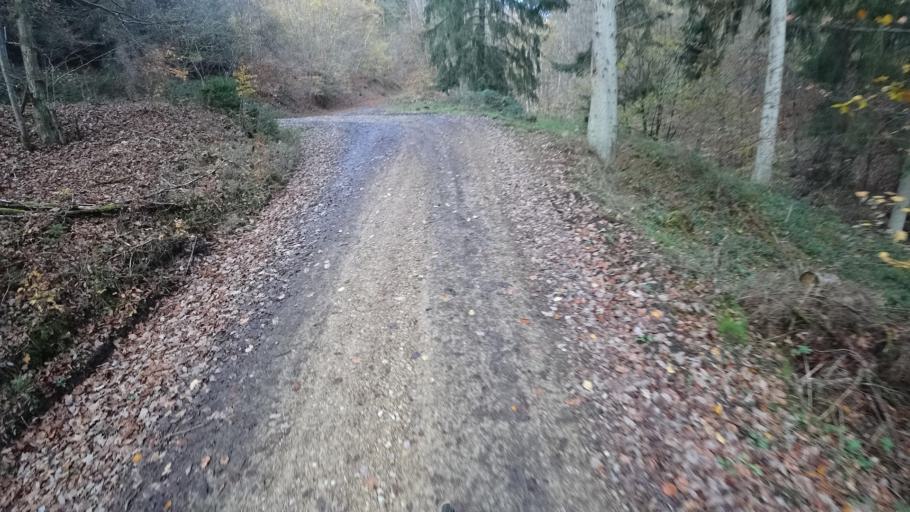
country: DE
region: Rheinland-Pfalz
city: Sierscheid
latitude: 50.4748
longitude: 6.9297
